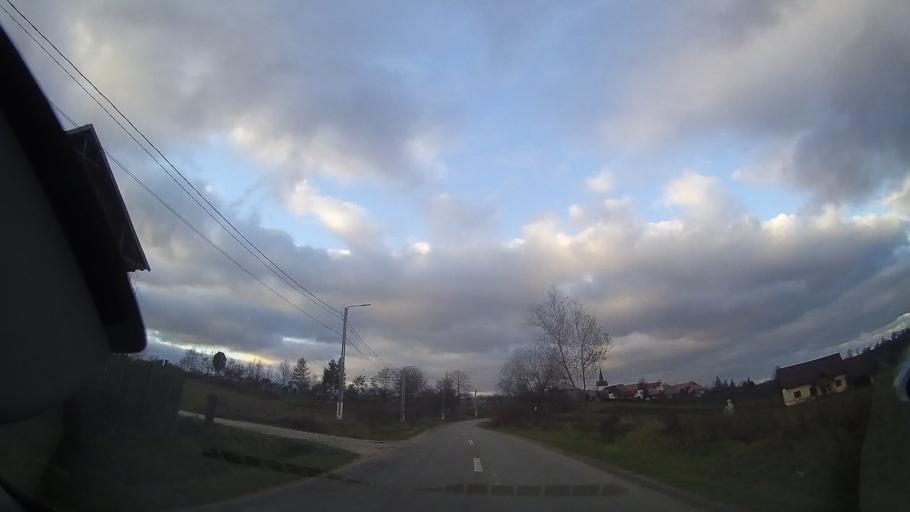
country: RO
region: Cluj
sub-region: Comuna Sancraiu
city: Sancraiu
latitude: 46.8260
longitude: 22.9901
